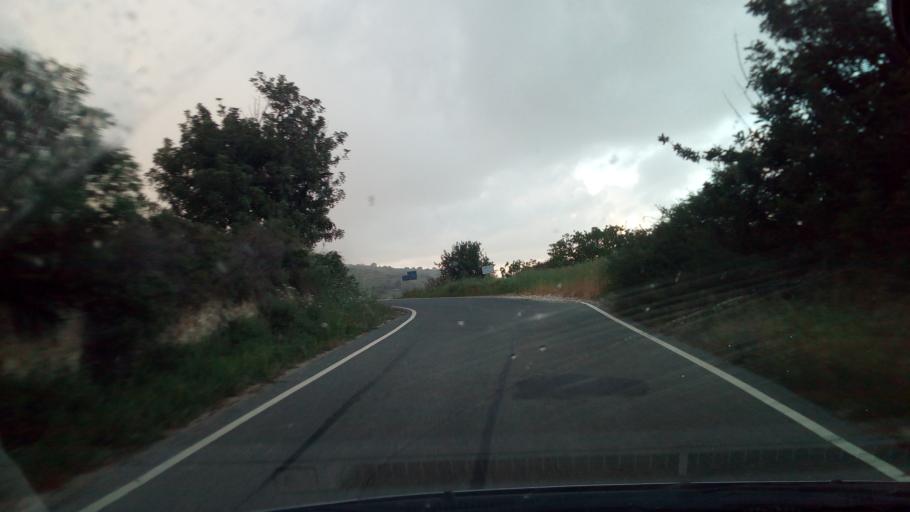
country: CY
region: Pafos
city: Polis
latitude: 34.9592
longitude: 32.4322
